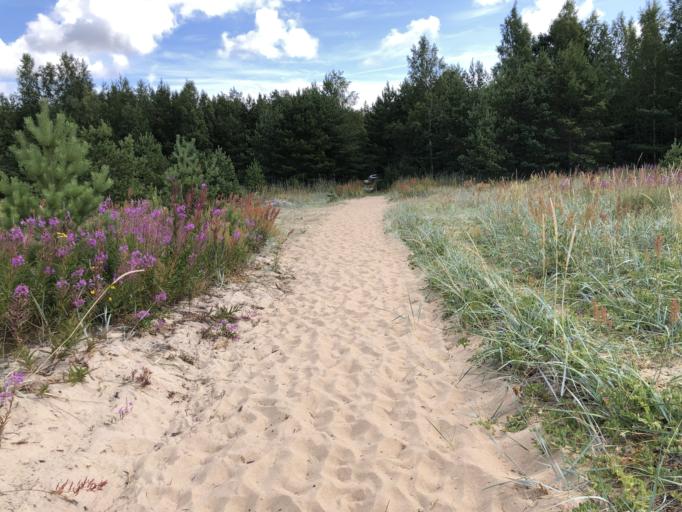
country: EE
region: Hiiumaa
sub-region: Kaerdla linn
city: Kardla
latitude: 59.0364
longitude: 22.5784
